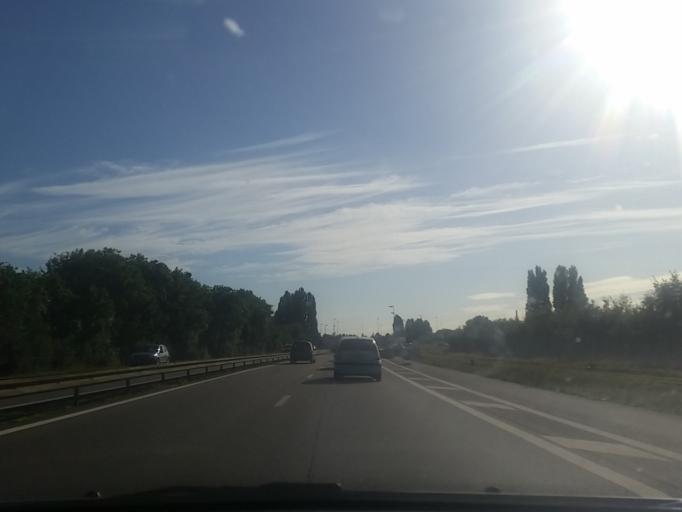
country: FR
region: Pays de la Loire
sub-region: Departement de la Loire-Atlantique
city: Reze
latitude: 47.1890
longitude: -1.5833
